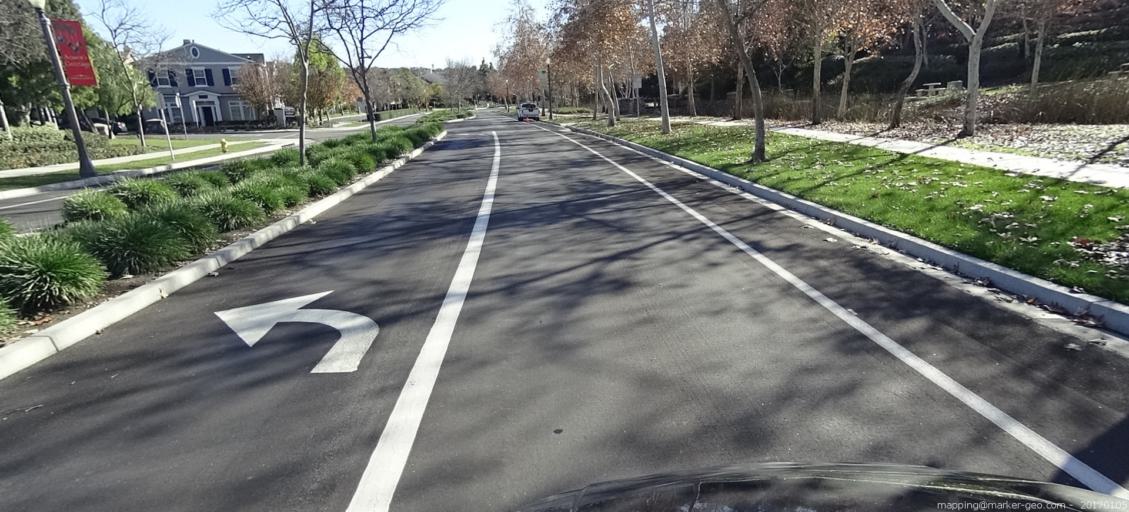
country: US
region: California
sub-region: Orange County
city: Ladera Ranch
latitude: 33.5506
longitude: -117.6384
